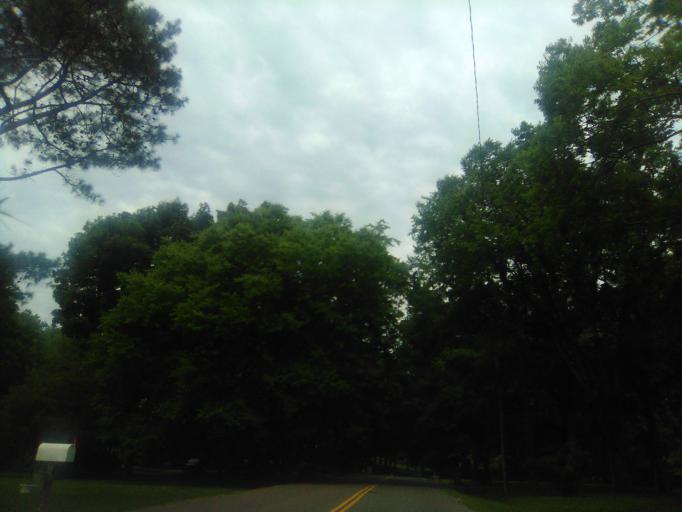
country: US
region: Tennessee
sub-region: Davidson County
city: Belle Meade
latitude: 36.1077
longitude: -86.8881
